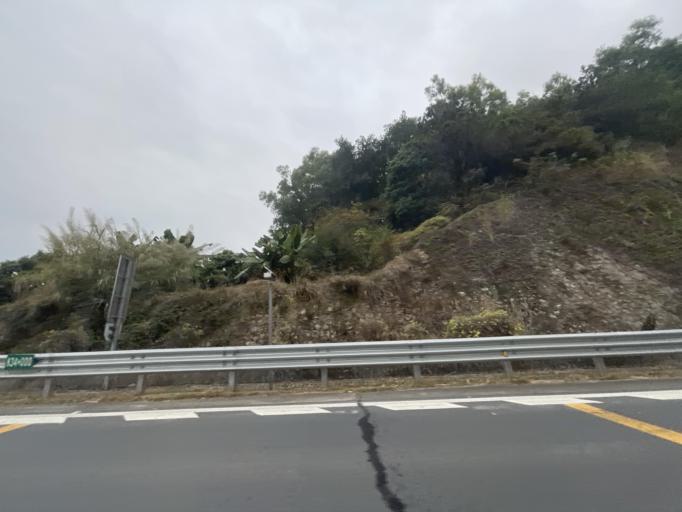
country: CN
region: Guangdong
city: Humen
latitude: 22.8067
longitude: 113.6531
